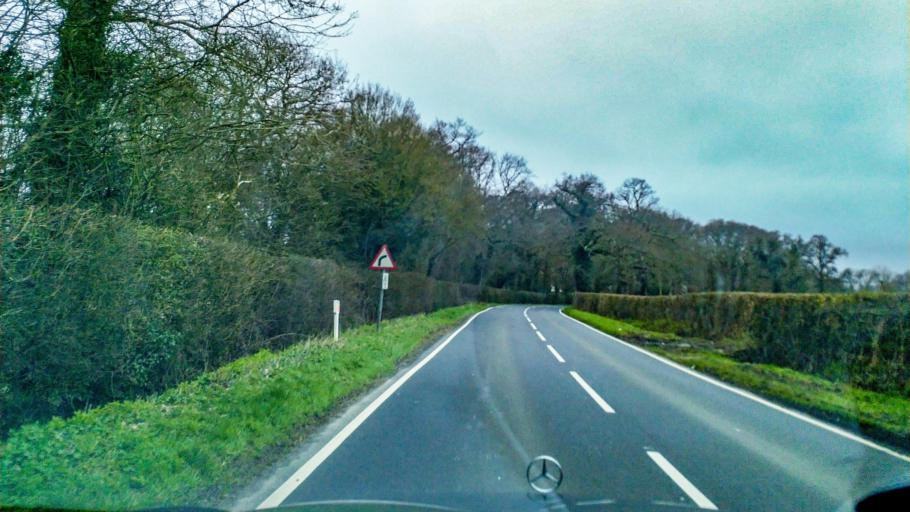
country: GB
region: England
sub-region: Surrey
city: Salfords
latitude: 51.1826
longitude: -0.2143
